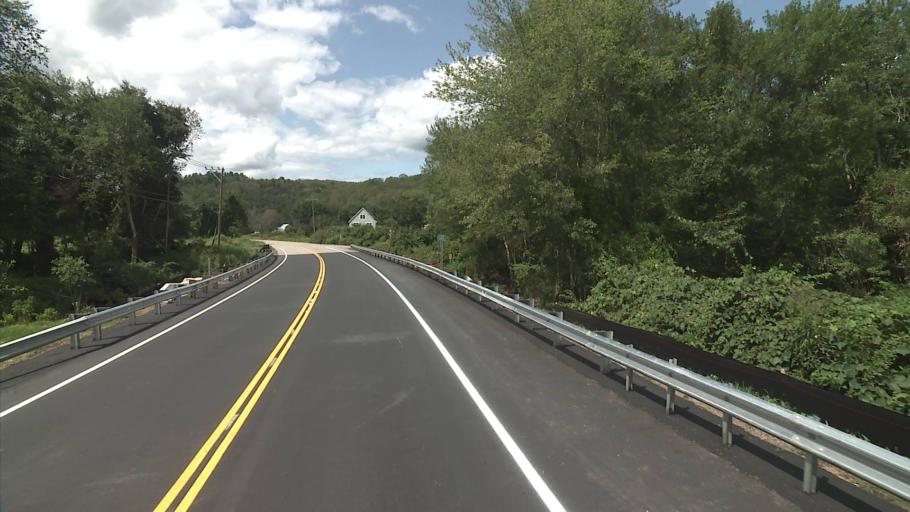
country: US
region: Connecticut
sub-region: New London County
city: Baltic
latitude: 41.6333
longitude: -72.1297
